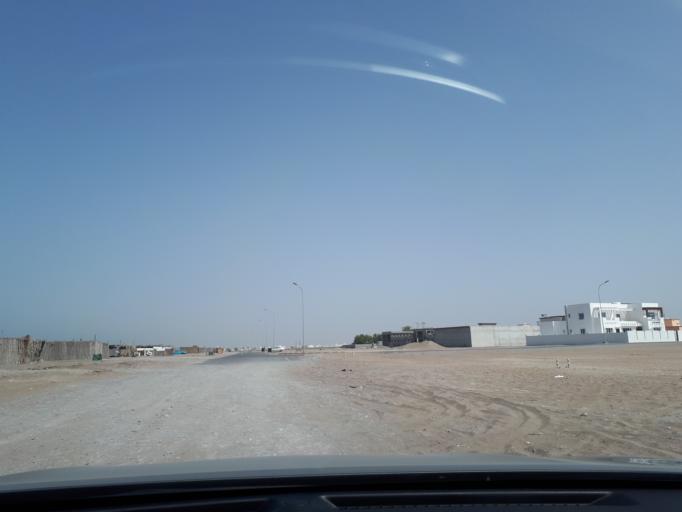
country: OM
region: Al Batinah
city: Barka'
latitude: 23.7298
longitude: 57.8381
